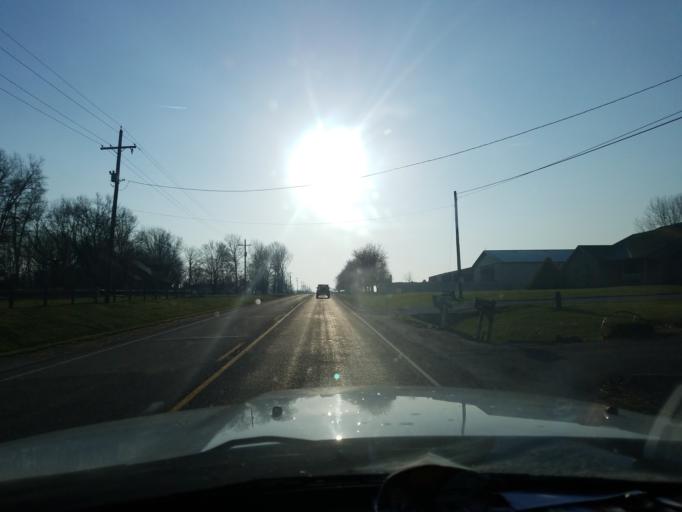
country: US
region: Indiana
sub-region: Vigo County
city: Seelyville
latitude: 39.3902
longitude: -87.2938
